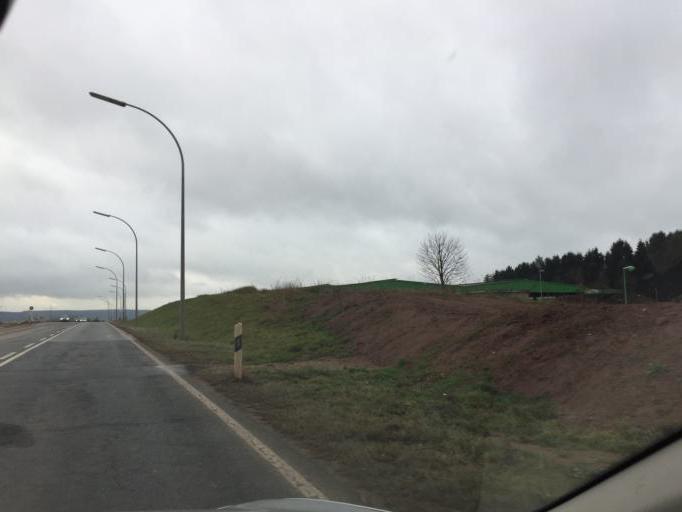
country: LU
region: Diekirch
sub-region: Canton de Diekirch
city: Diekirch
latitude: 49.8811
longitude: 6.1344
